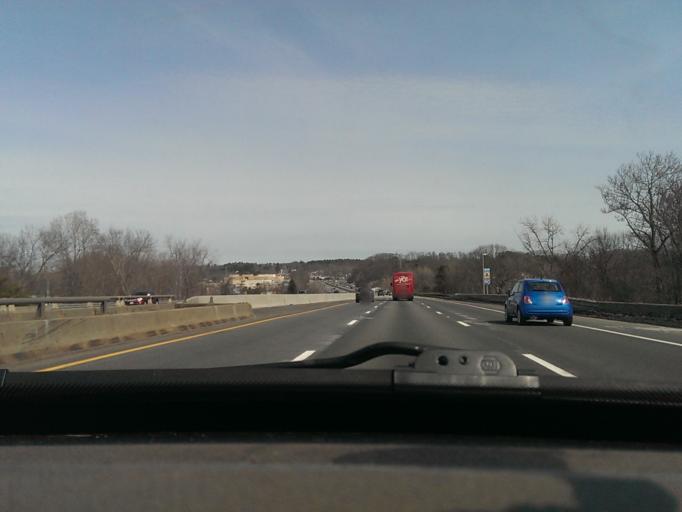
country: US
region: Massachusetts
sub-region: Worcester County
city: Auburn
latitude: 42.1945
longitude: -71.8475
